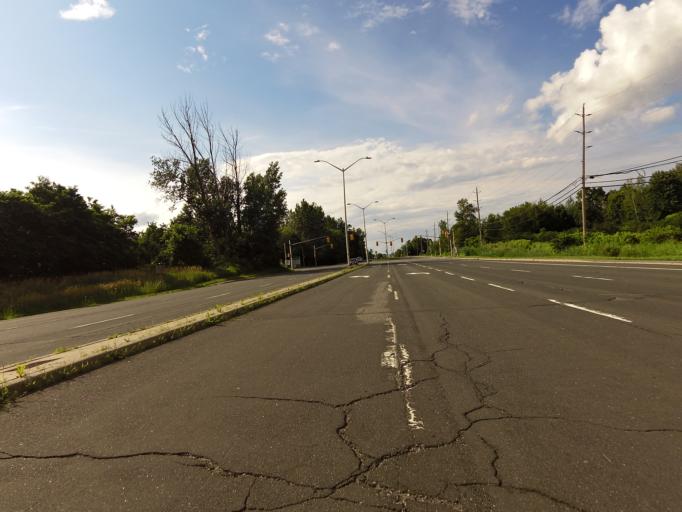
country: CA
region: Ontario
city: Bells Corners
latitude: 45.3465
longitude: -75.8440
